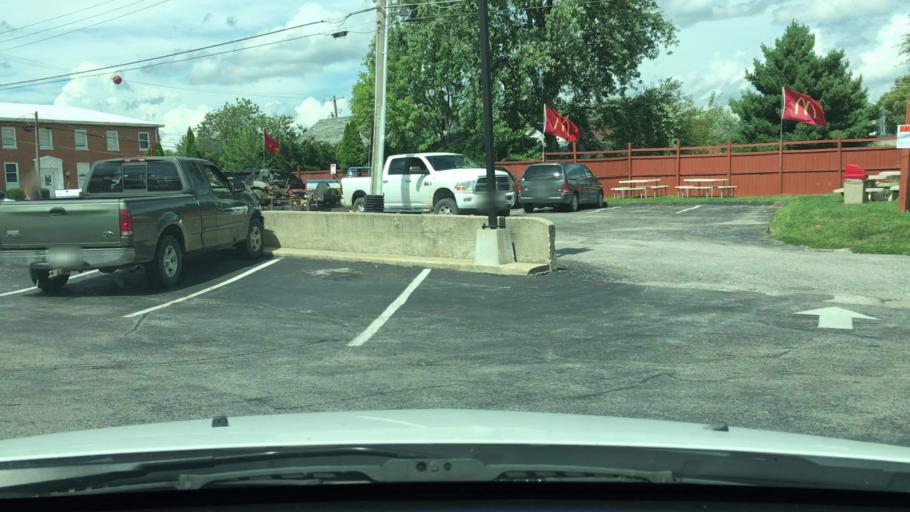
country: US
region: Illinois
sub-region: Pike County
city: Pittsfield
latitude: 39.6073
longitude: -90.8132
